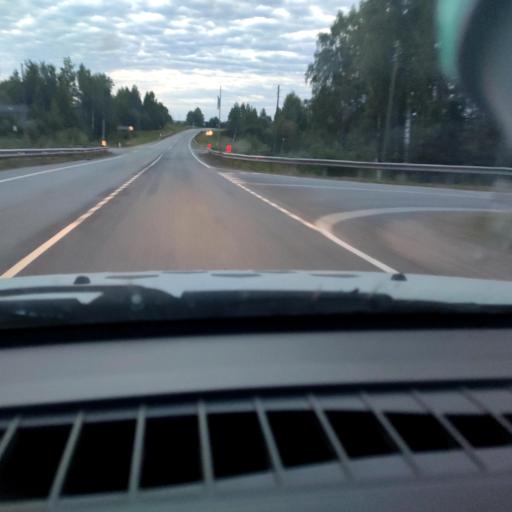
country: RU
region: Kirov
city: Torfyanoy
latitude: 58.7176
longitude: 49.2129
